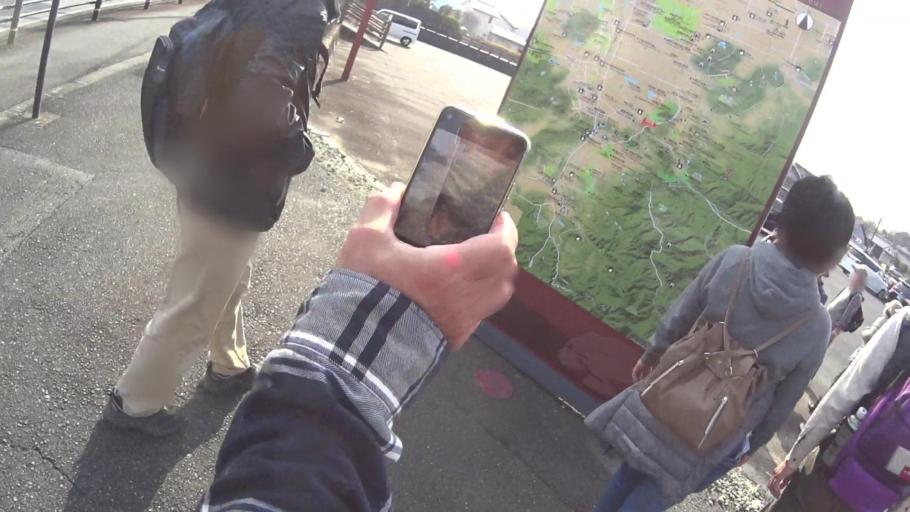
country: JP
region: Nara
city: Kashihara-shi
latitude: 34.4712
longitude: 135.8093
